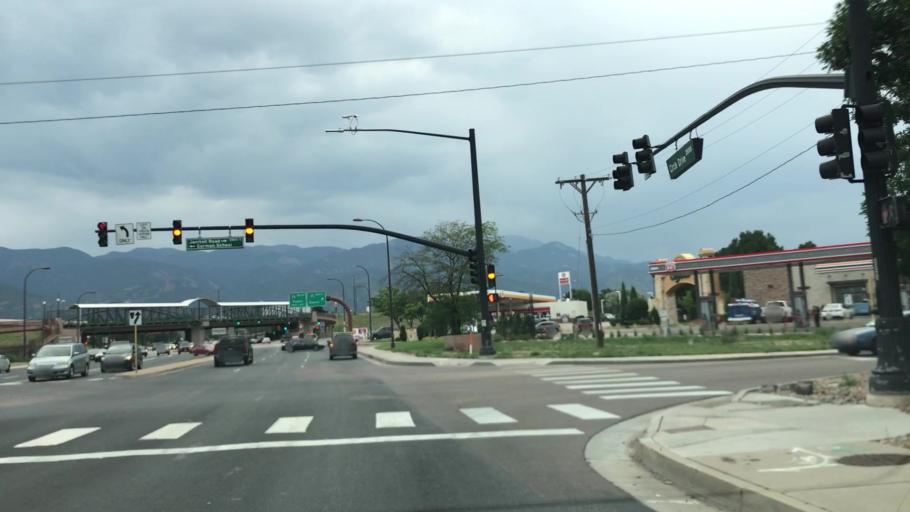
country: US
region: Colorado
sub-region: El Paso County
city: Stratmoor
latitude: 38.7963
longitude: -104.7942
